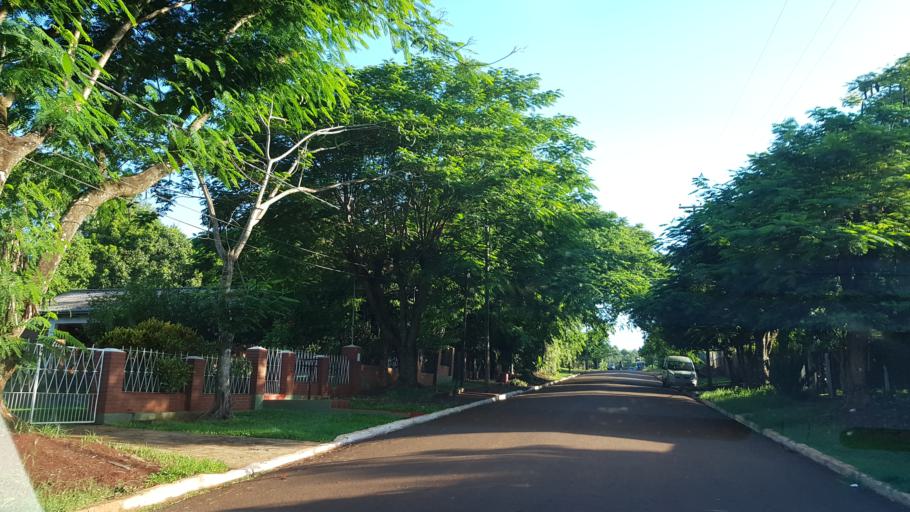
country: AR
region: Misiones
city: Puerto Libertad
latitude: -25.9210
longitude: -54.5871
